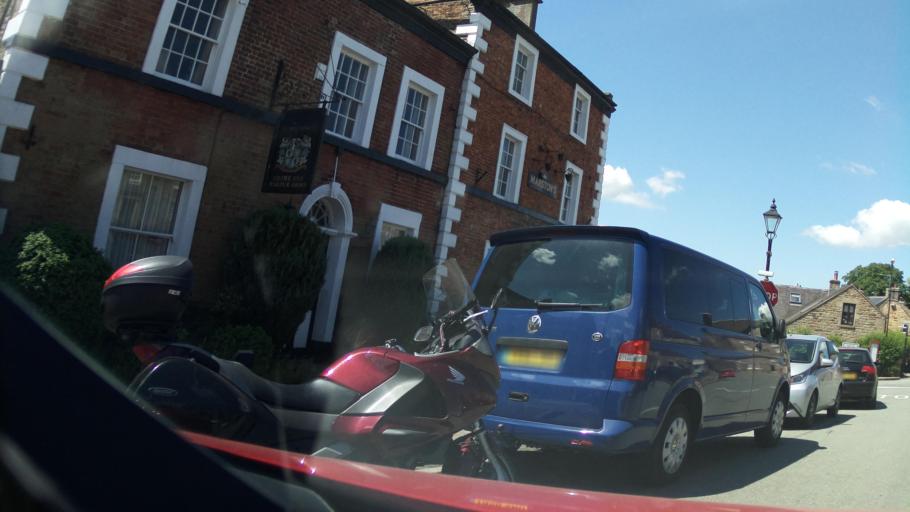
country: GB
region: England
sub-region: Derbyshire
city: Buxton
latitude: 53.1812
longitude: -1.8685
